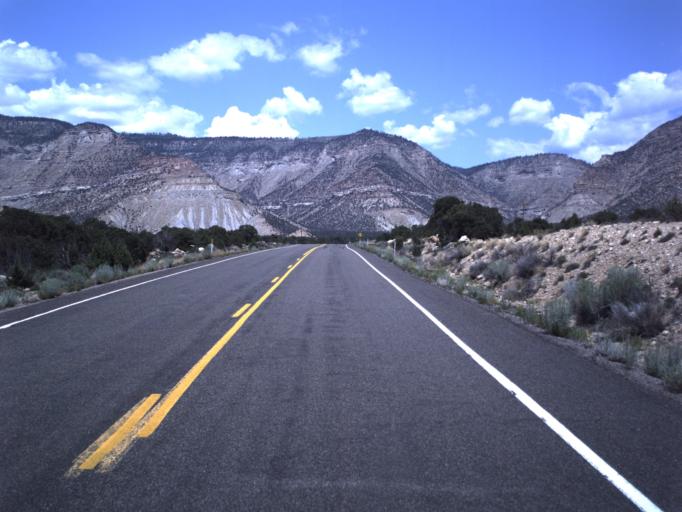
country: US
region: Utah
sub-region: Emery County
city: Orangeville
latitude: 39.2807
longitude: -111.1025
